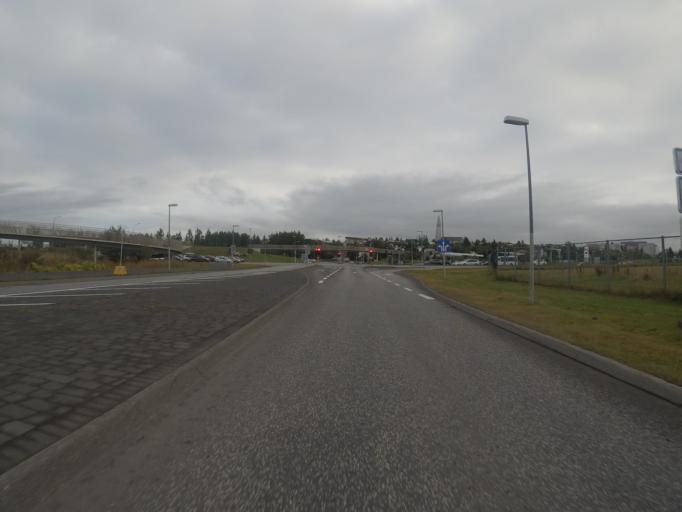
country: IS
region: Capital Region
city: Kopavogur
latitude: 64.1380
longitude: -21.9412
